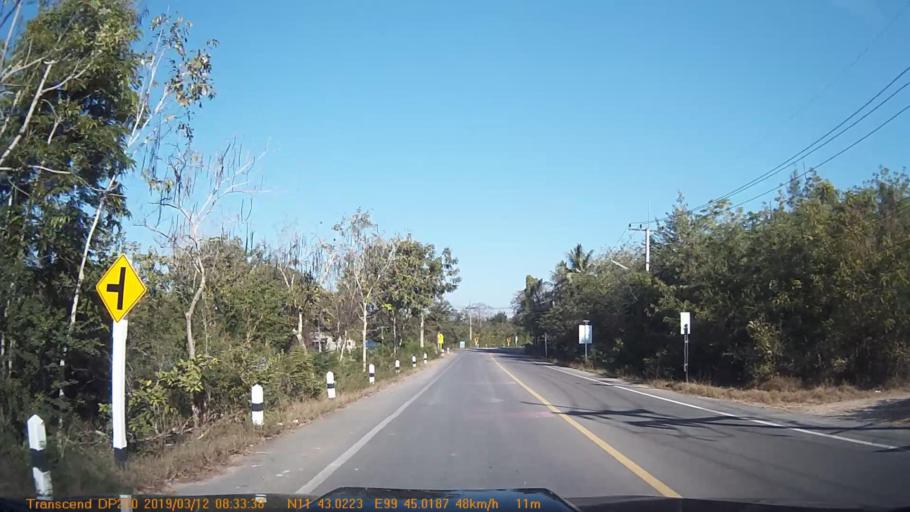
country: TH
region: Prachuap Khiri Khan
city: Prachuap Khiri Khan
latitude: 11.7171
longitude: 99.7502
